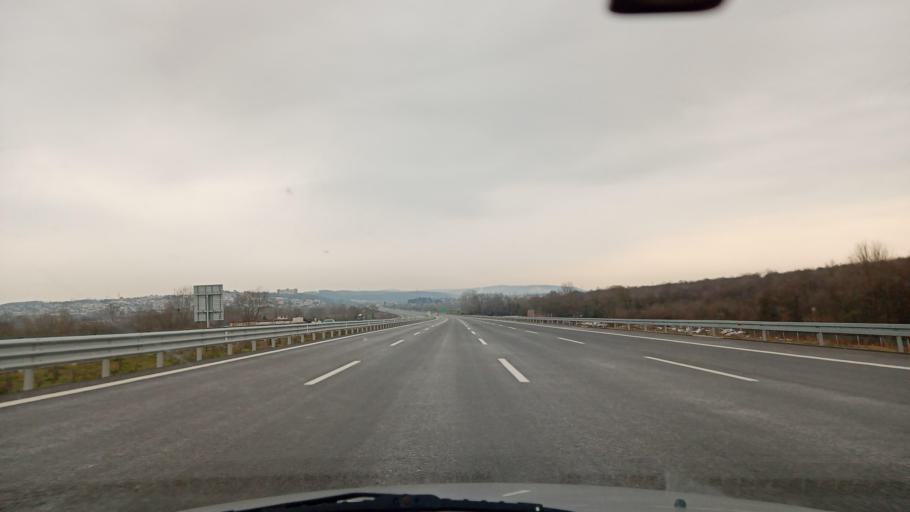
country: TR
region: Sakarya
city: Kazimpasa
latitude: 40.8433
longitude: 30.3023
